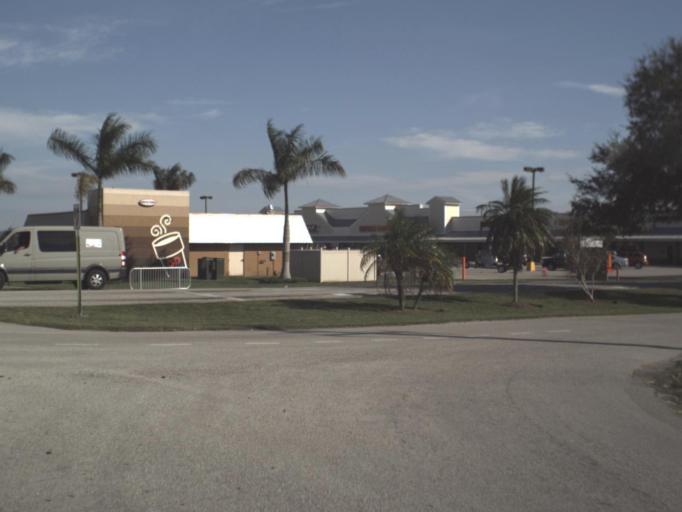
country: US
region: Florida
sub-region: Hendry County
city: Clewiston
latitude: 26.7541
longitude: -80.9473
